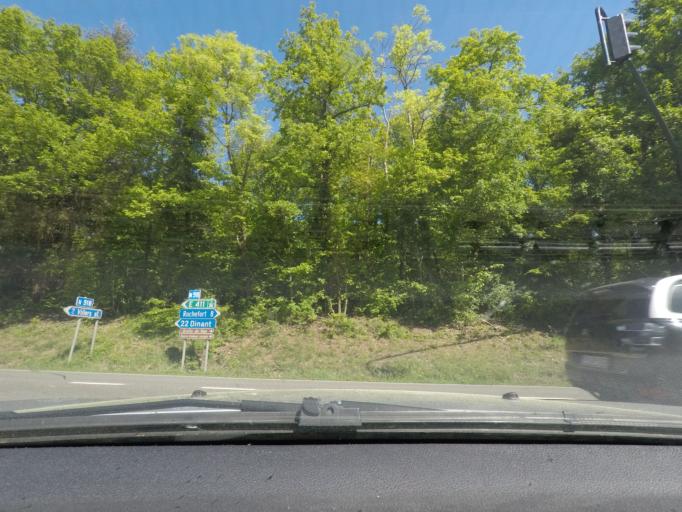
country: BE
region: Wallonia
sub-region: Province du Luxembourg
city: Wellin
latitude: 50.1710
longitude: 5.1142
